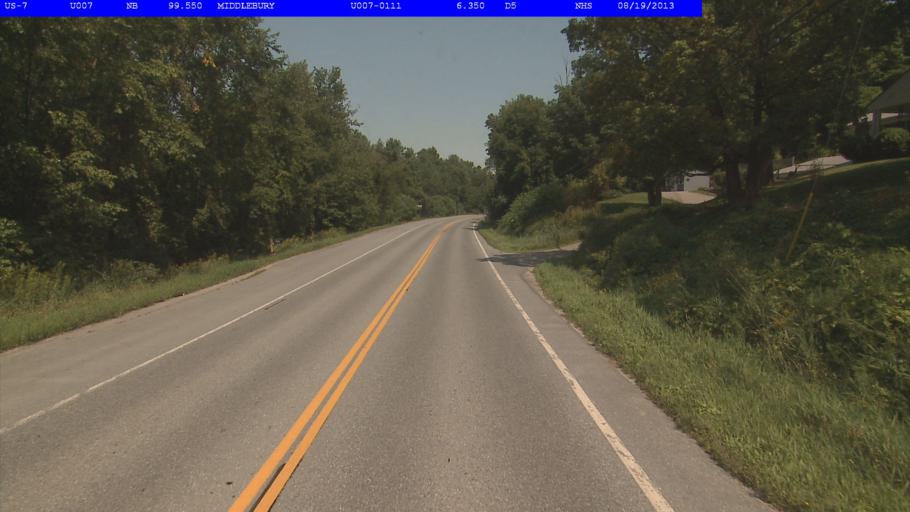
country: US
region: Vermont
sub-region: Addison County
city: Middlebury (village)
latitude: 44.0318
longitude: -73.1662
